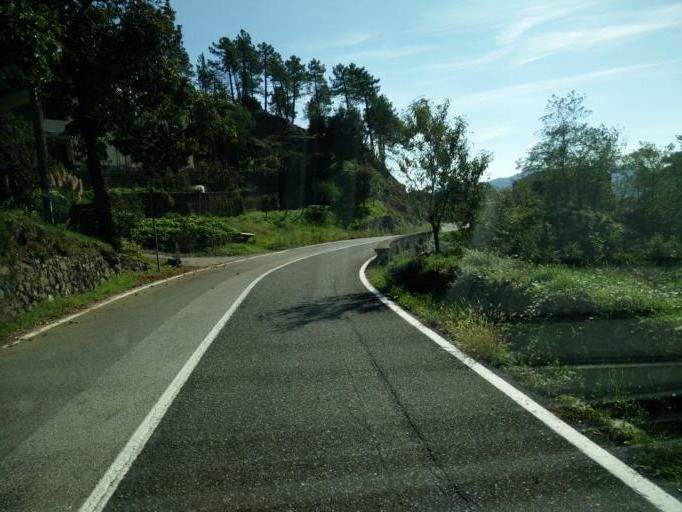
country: IT
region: Liguria
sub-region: Provincia di La Spezia
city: Carrodano
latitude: 44.2483
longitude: 9.6138
